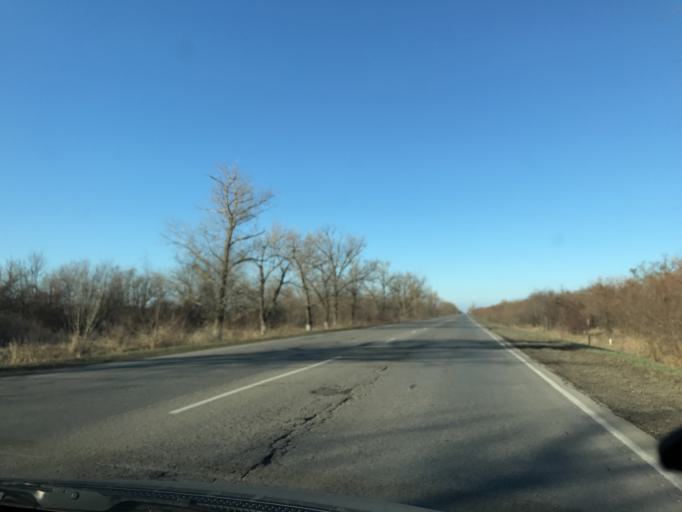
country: RU
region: Rostov
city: Kirovskaya
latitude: 47.0188
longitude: 39.9032
